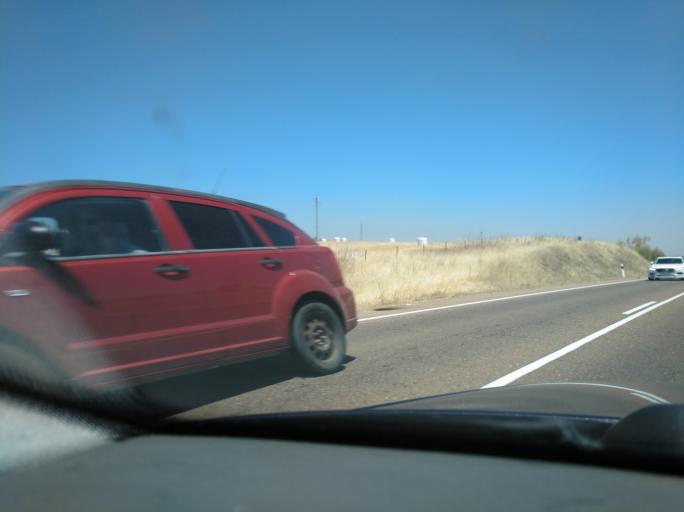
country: ES
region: Extremadura
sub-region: Provincia de Badajoz
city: Olivenza
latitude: 38.7281
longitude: -7.0746
